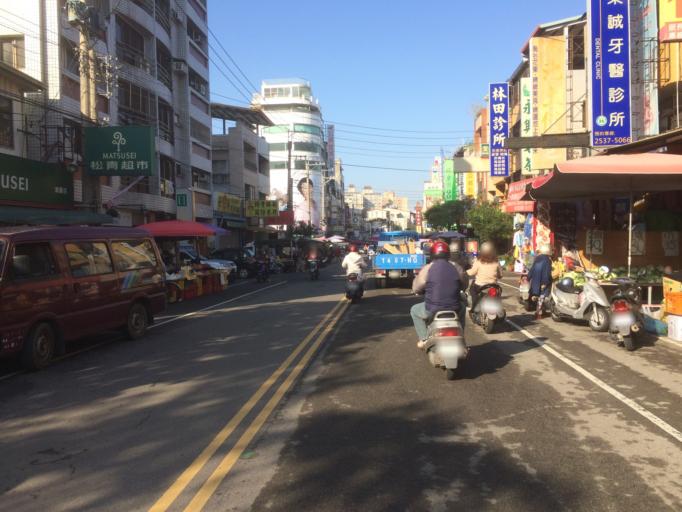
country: TW
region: Taiwan
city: Fengyuan
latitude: 24.2105
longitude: 120.7100
